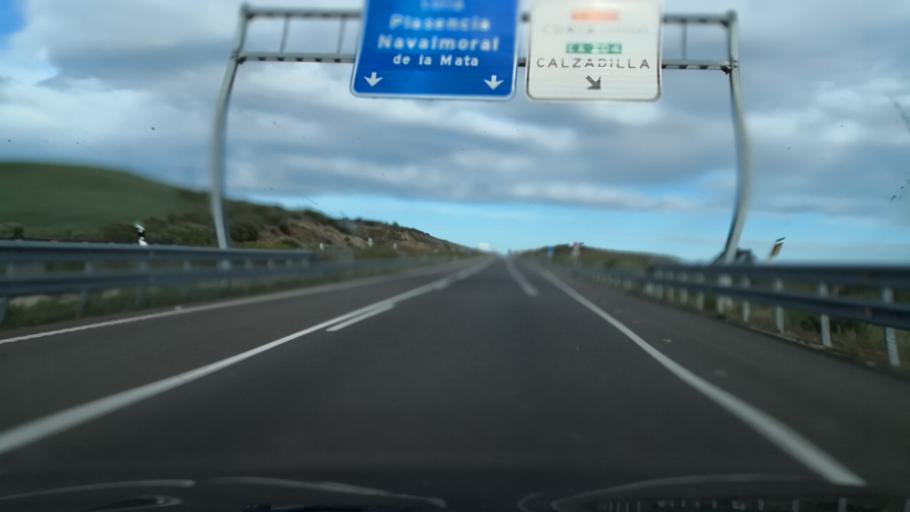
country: ES
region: Extremadura
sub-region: Provincia de Caceres
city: Casas de Don Gomez
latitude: 40.0111
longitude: -6.5676
